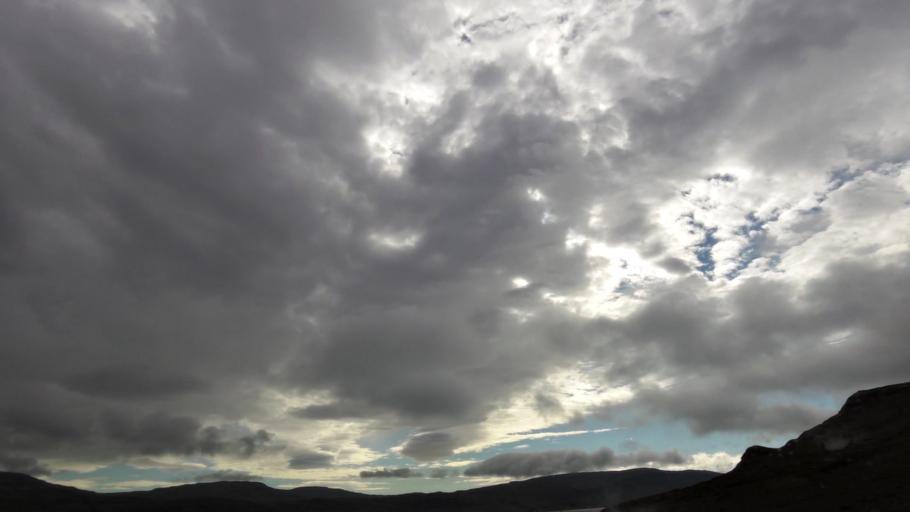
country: IS
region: West
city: Olafsvik
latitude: 65.5382
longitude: -23.8487
